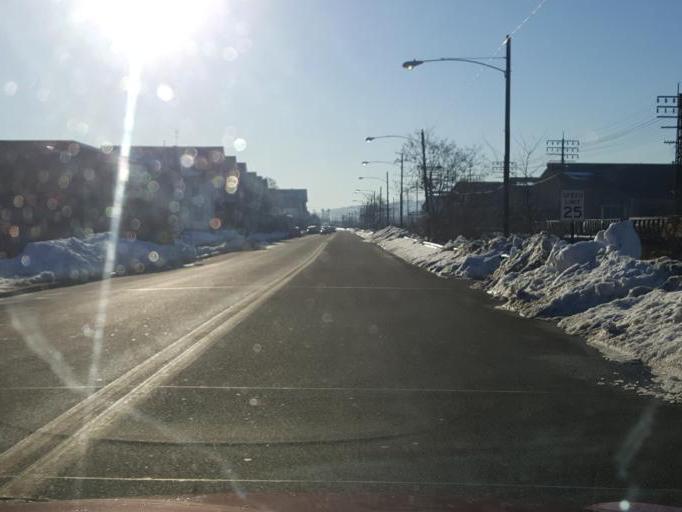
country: US
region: Pennsylvania
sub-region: Dauphin County
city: Enhaut
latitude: 40.2290
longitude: -76.8323
